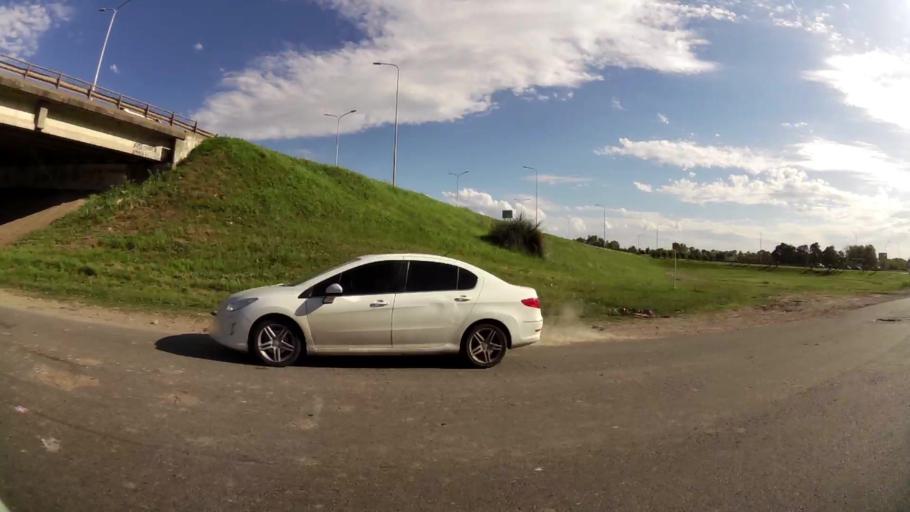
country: AR
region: Buenos Aires
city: Hurlingham
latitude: -34.5629
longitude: -58.6288
